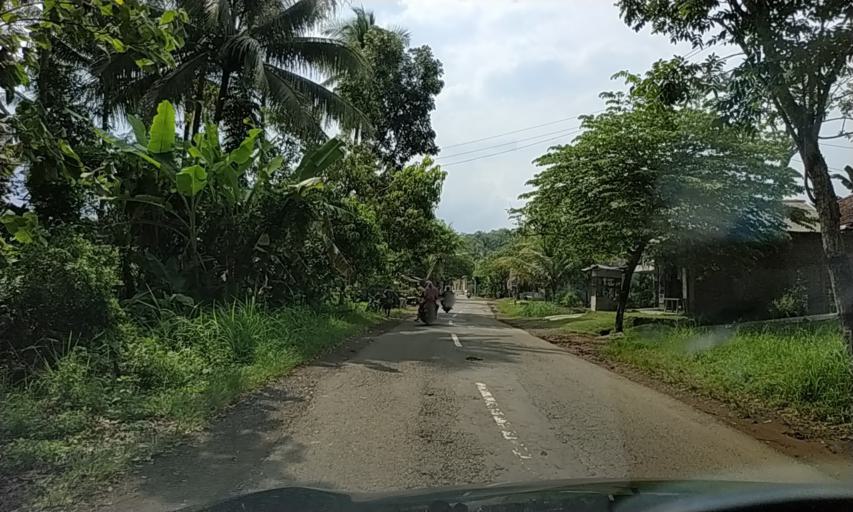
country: ID
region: Central Java
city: Winangun
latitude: -7.3746
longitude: 108.7008
